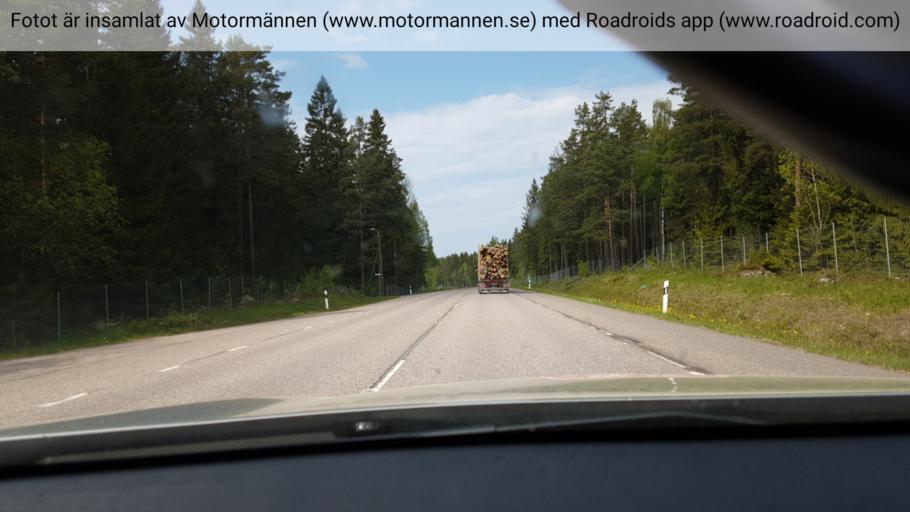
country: SE
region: Uppsala
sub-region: Alvkarleby Kommun
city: AElvkarleby
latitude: 60.5941
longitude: 17.4621
